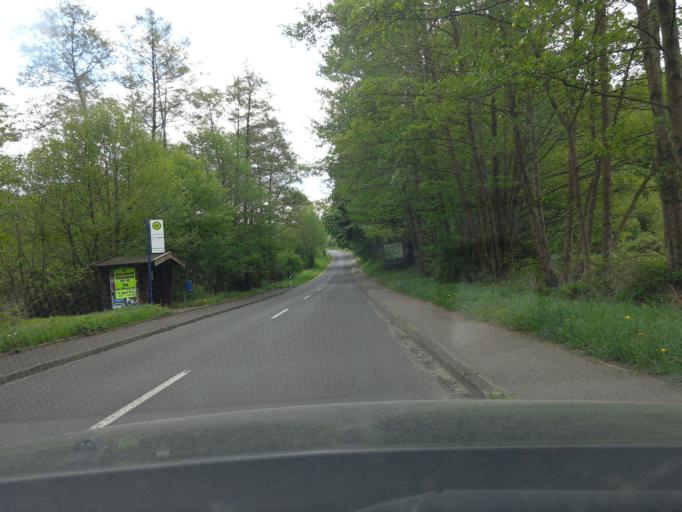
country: DE
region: Hesse
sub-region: Regierungsbezirk Darmstadt
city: Bad Orb
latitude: 50.2108
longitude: 9.3733
